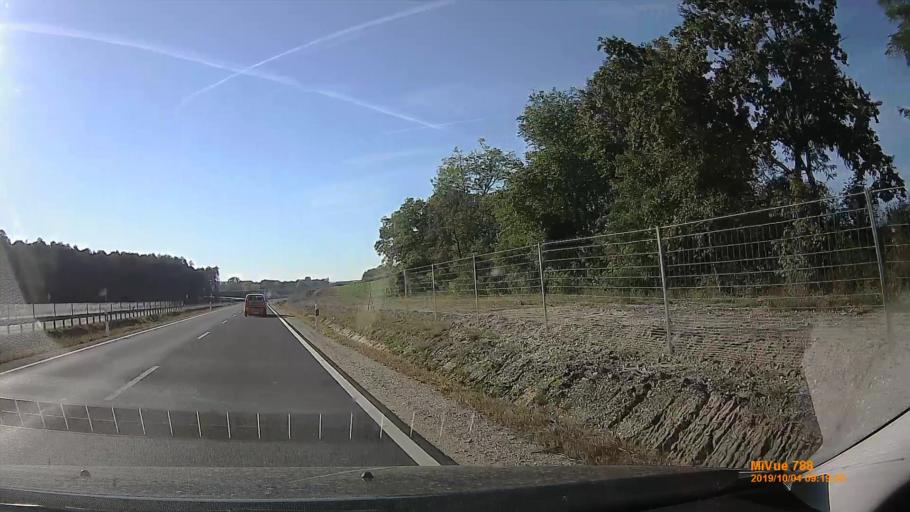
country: HU
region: Somogy
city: Karad
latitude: 46.5831
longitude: 17.8037
